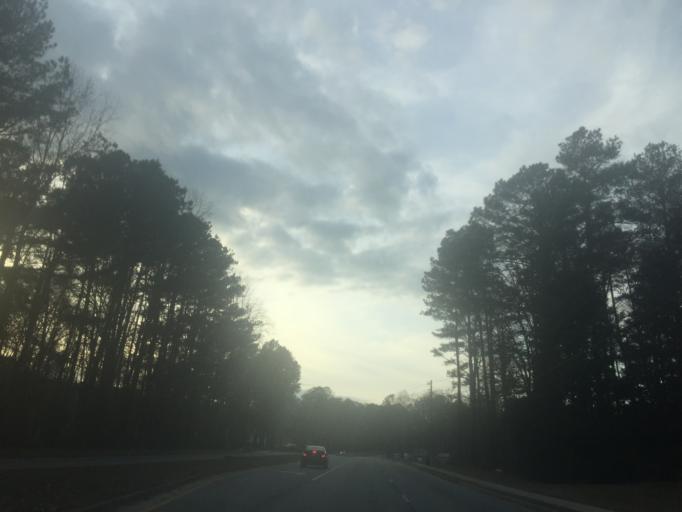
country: US
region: Georgia
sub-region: Clayton County
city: Riverdale
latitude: 33.5945
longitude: -84.4113
